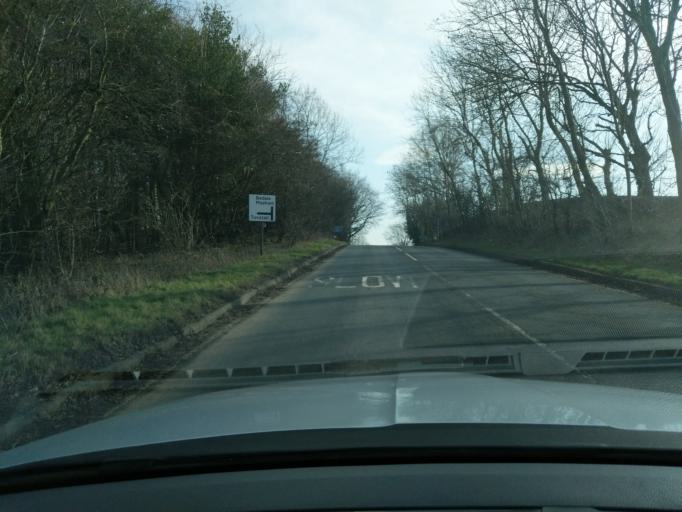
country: GB
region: England
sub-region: North Yorkshire
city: Catterick Garrison
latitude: 54.3489
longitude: -1.6949
